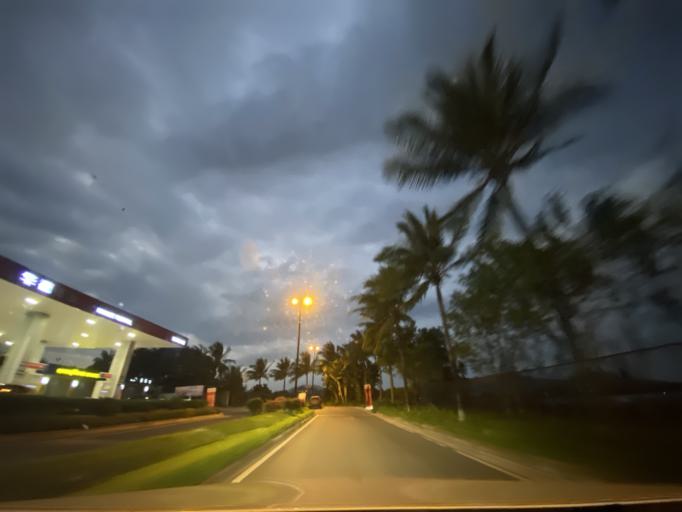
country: CN
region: Hainan
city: Yingzhou
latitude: 18.4148
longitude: 109.8789
